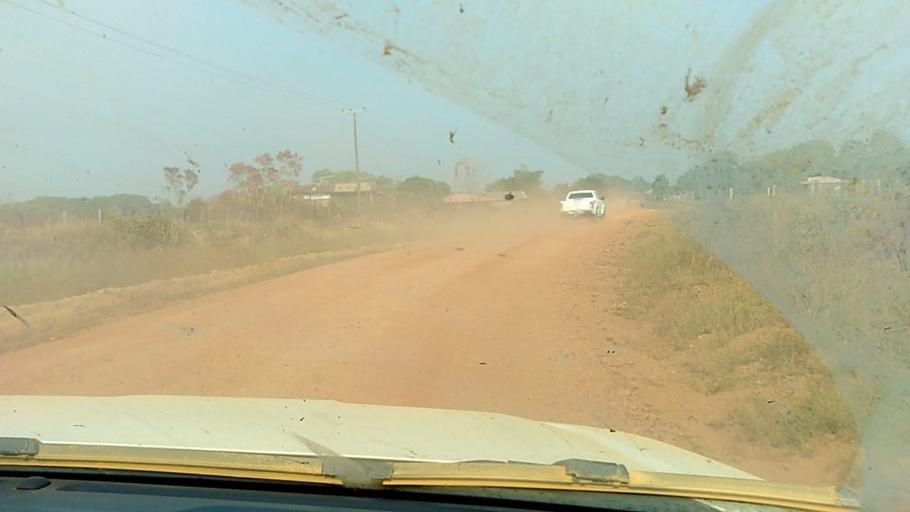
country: BR
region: Rondonia
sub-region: Porto Velho
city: Porto Velho
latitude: -8.7674
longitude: -64.0720
